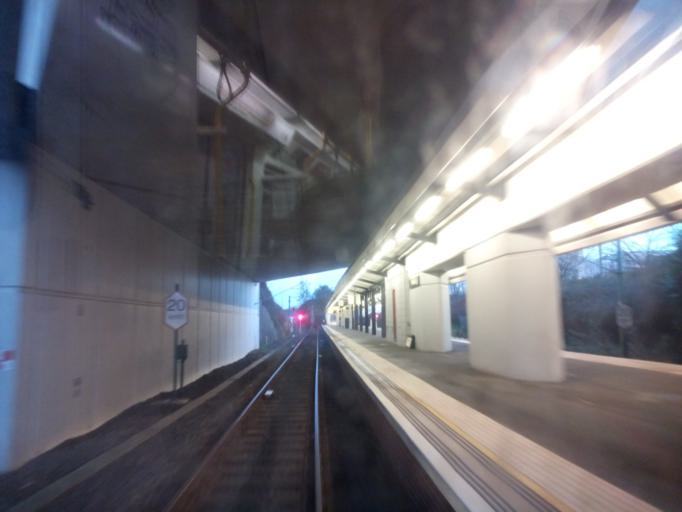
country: GB
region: England
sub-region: Northumberland
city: Ponteland
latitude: 55.0351
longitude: -1.7109
